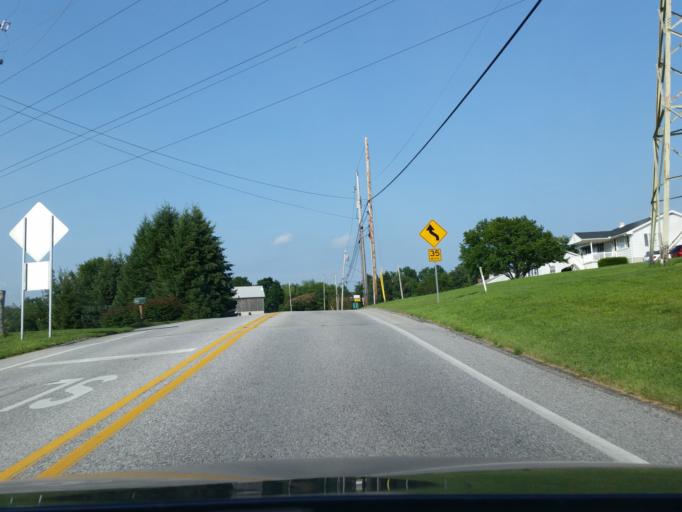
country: US
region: Pennsylvania
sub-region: York County
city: Shiloh
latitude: 40.0022
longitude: -76.7700
